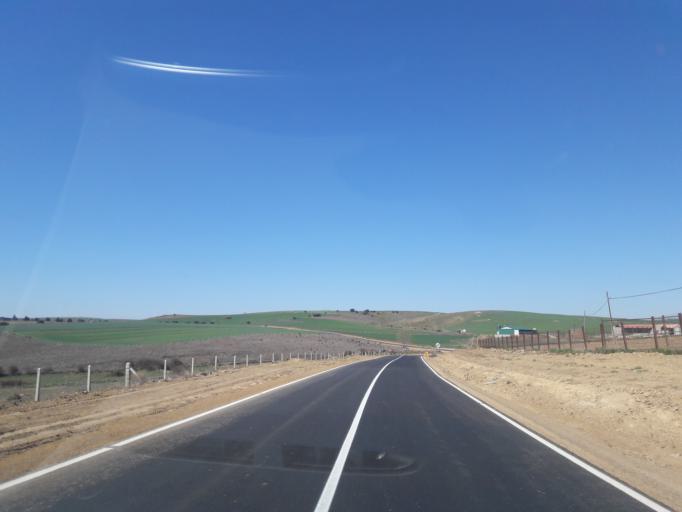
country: ES
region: Castille and Leon
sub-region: Provincia de Salamanca
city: Terradillos
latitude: 40.8258
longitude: -5.5445
